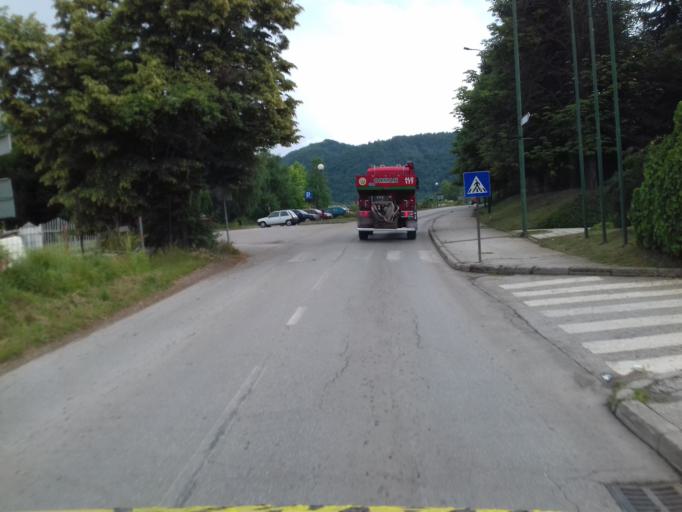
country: BA
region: Federation of Bosnia and Herzegovina
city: Visoko
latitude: 43.9784
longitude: 18.1855
